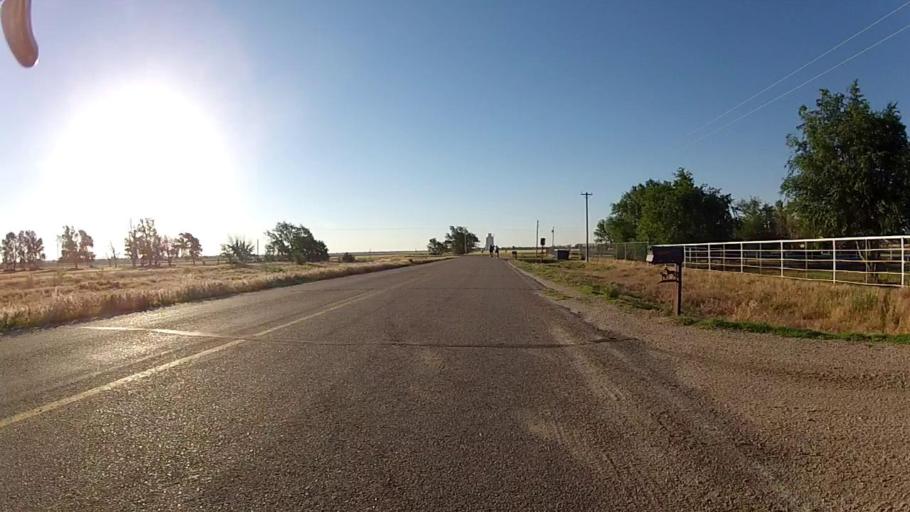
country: US
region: Kansas
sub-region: Ford County
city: Dodge City
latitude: 37.7070
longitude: -99.9078
